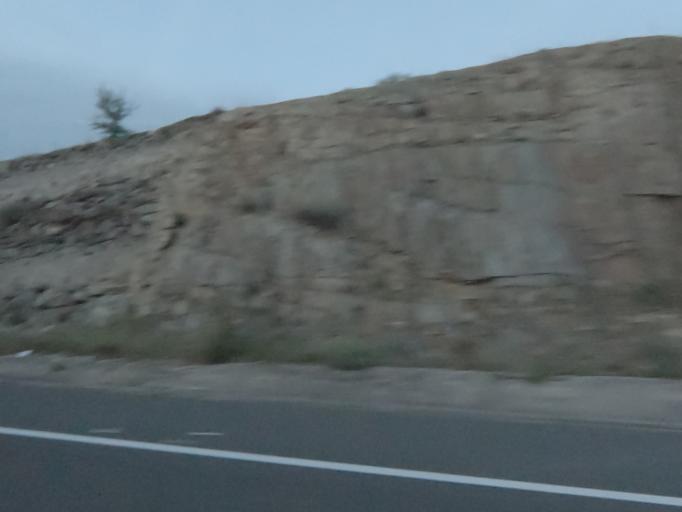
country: ES
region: Extremadura
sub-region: Provincia de Caceres
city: Hinojal
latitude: 39.7036
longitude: -6.4050
